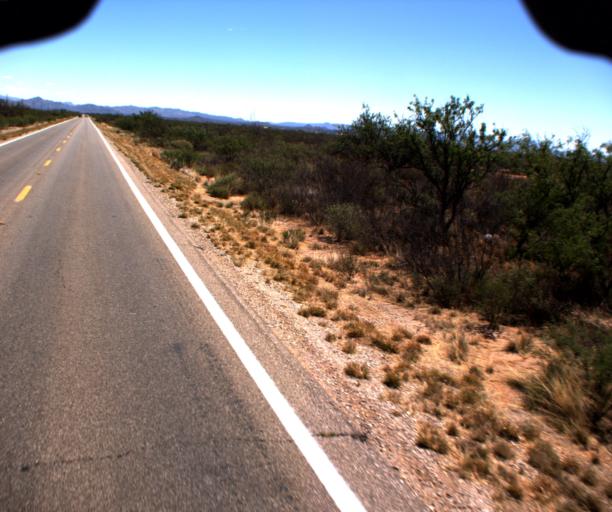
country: US
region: Arizona
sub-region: Cochise County
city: Huachuca City
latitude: 31.6932
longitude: -110.3308
